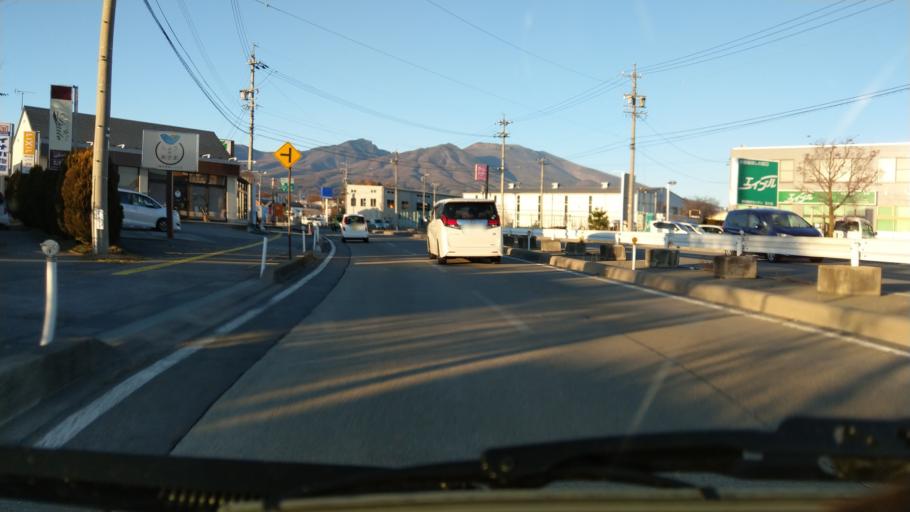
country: JP
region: Nagano
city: Komoro
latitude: 36.2859
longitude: 138.4743
